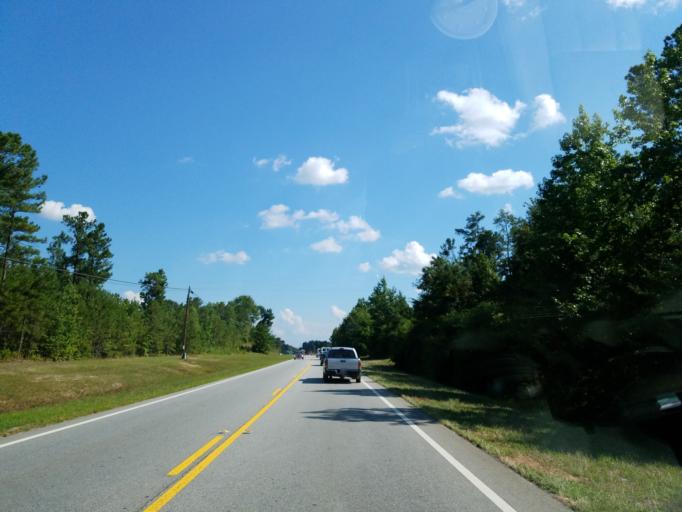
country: US
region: Georgia
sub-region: Crawford County
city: Roberta
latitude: 32.7420
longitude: -84.0167
